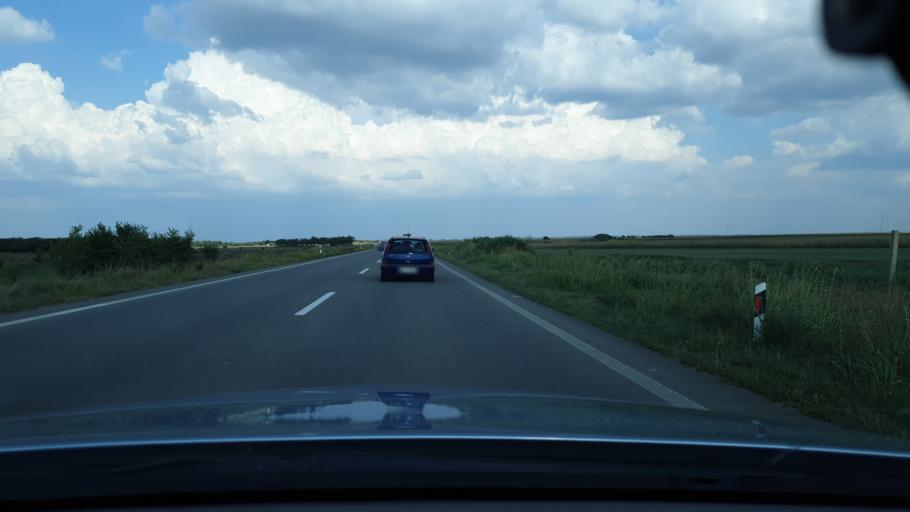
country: RS
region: Autonomna Pokrajina Vojvodina
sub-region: Juznobacki Okrug
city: Zabalj
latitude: 45.3654
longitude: 20.1005
